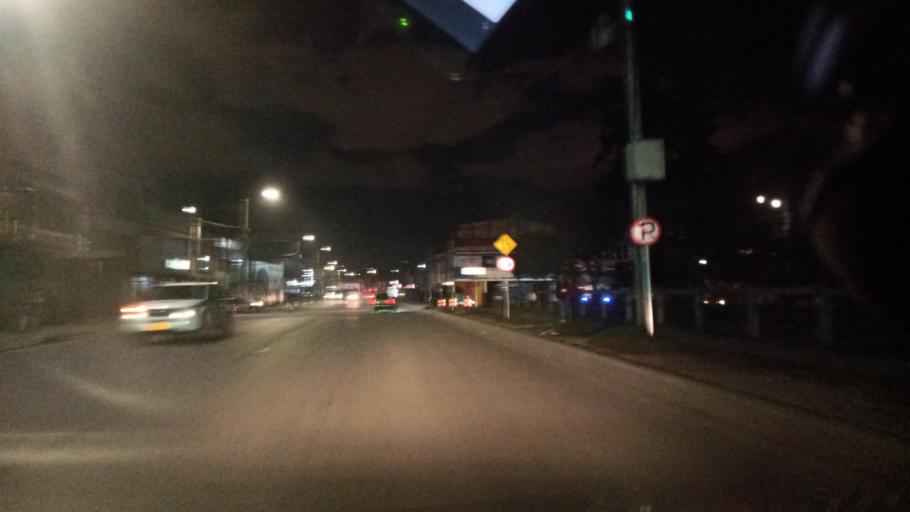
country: CO
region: Cundinamarca
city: Funza
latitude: 4.6800
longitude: -74.1523
